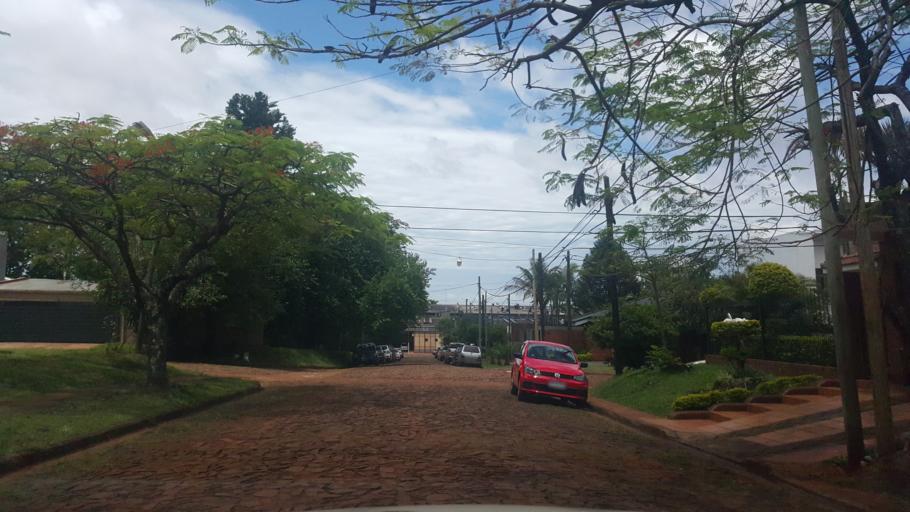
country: AR
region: Misiones
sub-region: Departamento de Capital
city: Posadas
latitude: -27.3976
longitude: -55.9107
